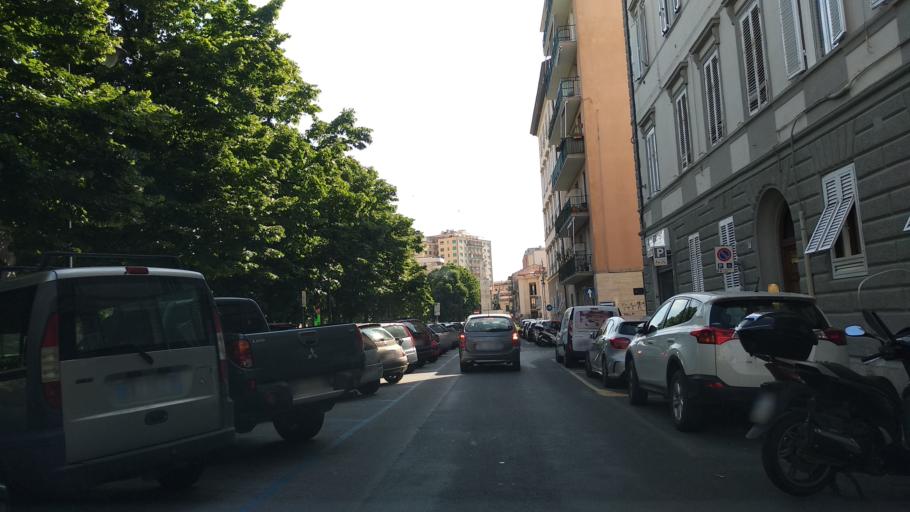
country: IT
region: Tuscany
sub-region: Provincia di Livorno
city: Livorno
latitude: 43.5469
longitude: 10.3167
